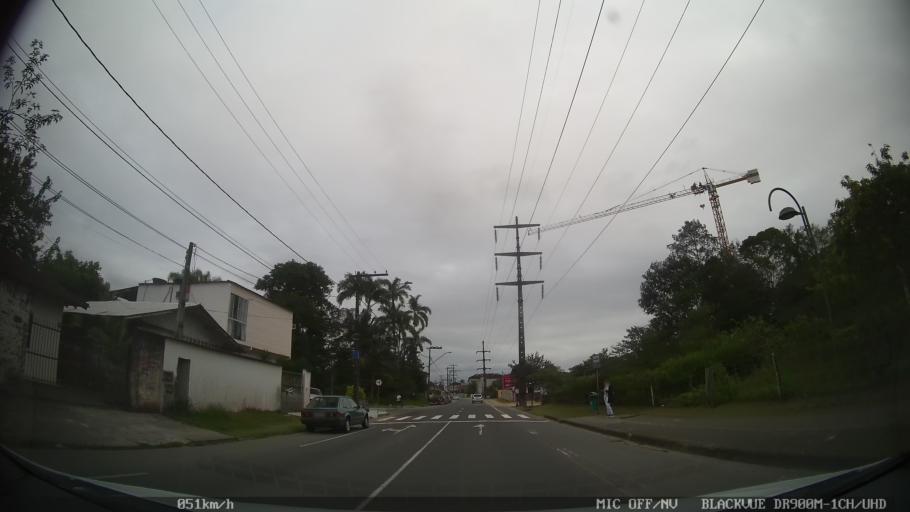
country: BR
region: Santa Catarina
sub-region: Joinville
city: Joinville
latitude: -26.2794
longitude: -48.8753
